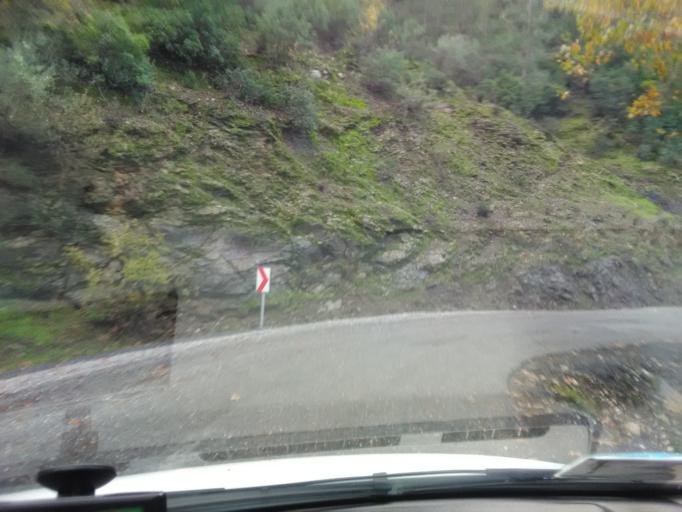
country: TR
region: Antalya
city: Gazipasa
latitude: 36.3027
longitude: 32.3911
